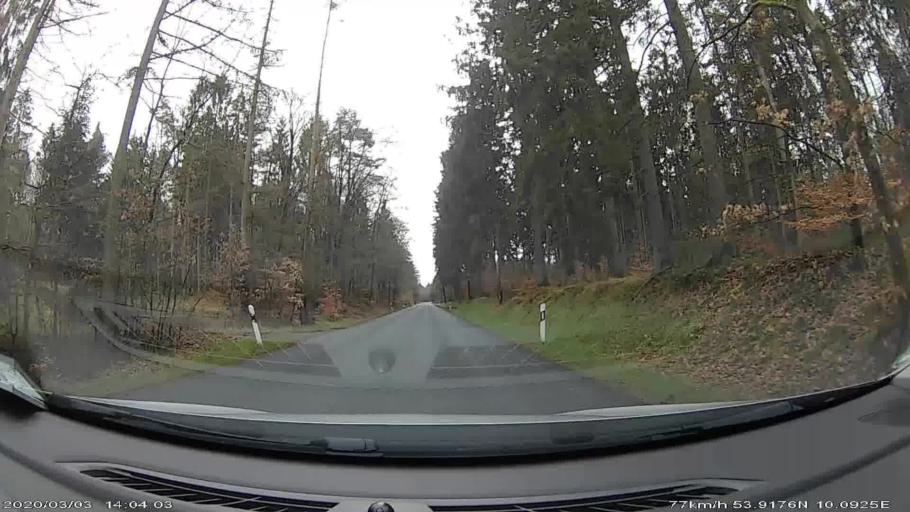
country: DE
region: Schleswig-Holstein
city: Hartenholm
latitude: 53.9168
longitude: 10.0925
